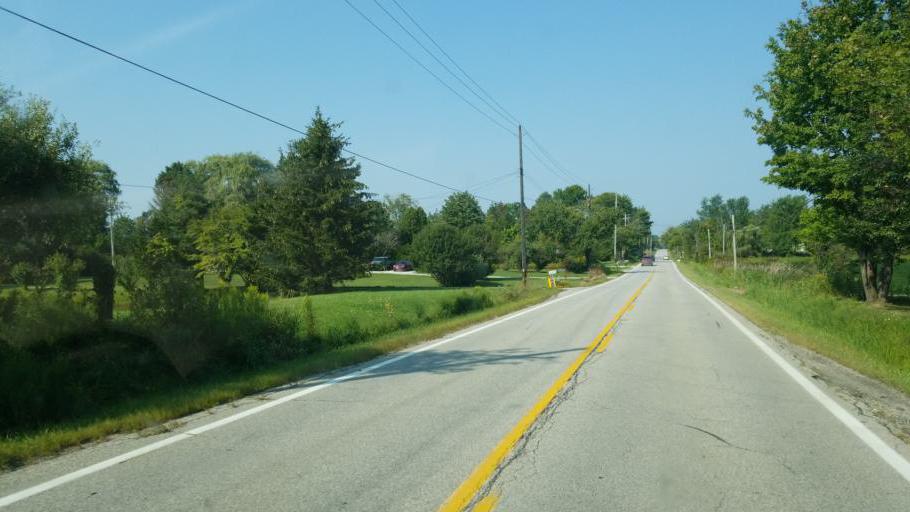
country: US
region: Ohio
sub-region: Geauga County
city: Chardon
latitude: 41.6074
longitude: -81.0796
